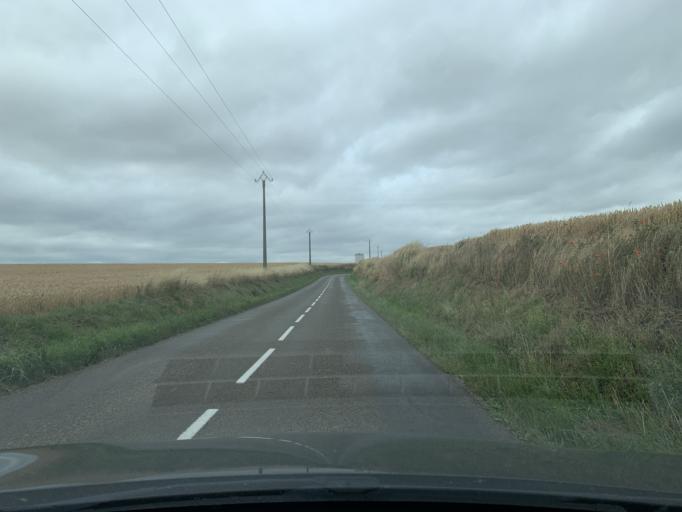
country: FR
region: Nord-Pas-de-Calais
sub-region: Departement du Nord
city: Neuville-Saint-Remy
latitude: 50.2257
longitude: 3.2185
